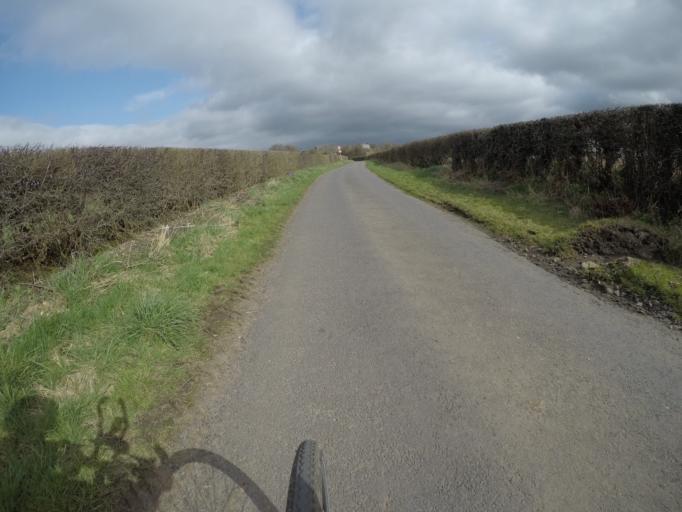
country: GB
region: Scotland
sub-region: North Ayrshire
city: Springside
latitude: 55.6469
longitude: -4.6200
